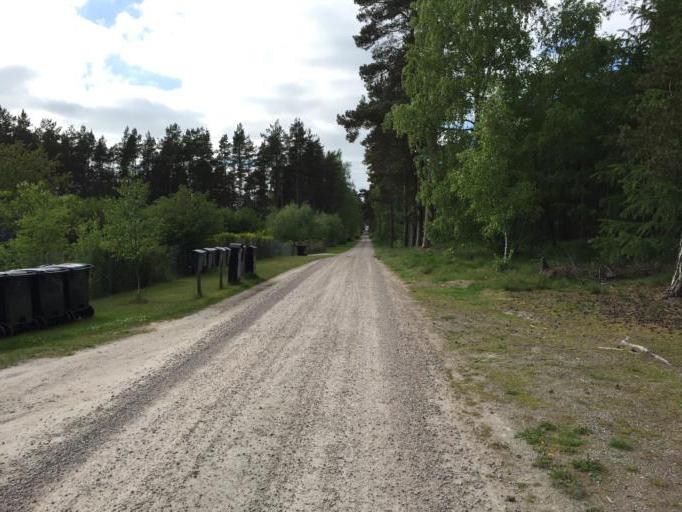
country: SE
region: Skane
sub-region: Sjobo Kommun
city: Sjoebo
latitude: 55.6661
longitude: 13.6345
